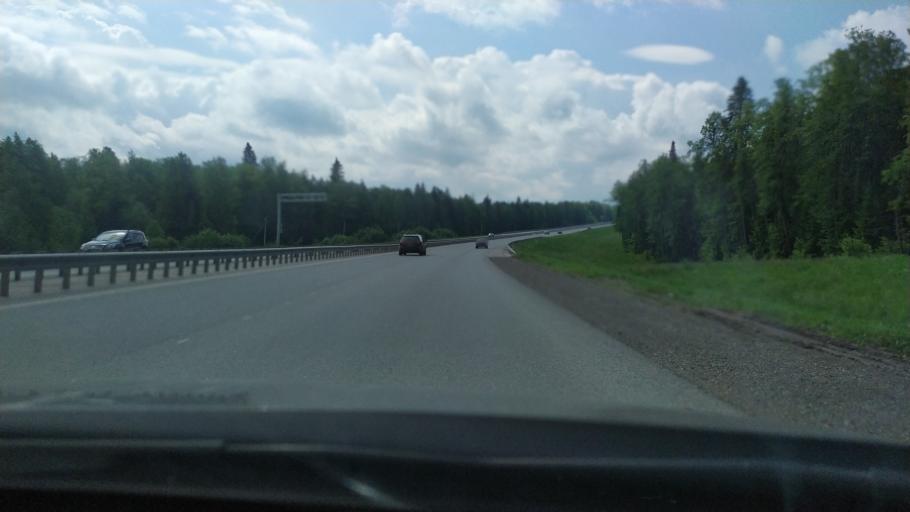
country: RU
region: Perm
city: Novyye Lyady
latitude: 58.0320
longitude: 56.4335
